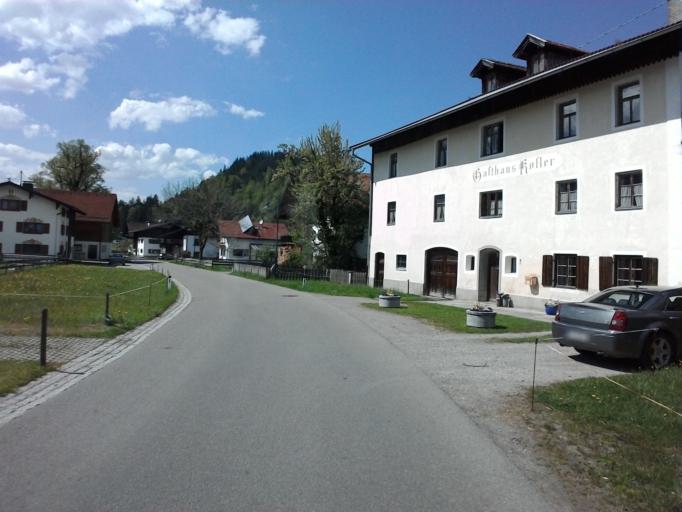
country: AT
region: Tyrol
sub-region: Politischer Bezirk Reutte
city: Musau
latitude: 47.5435
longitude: 10.6756
